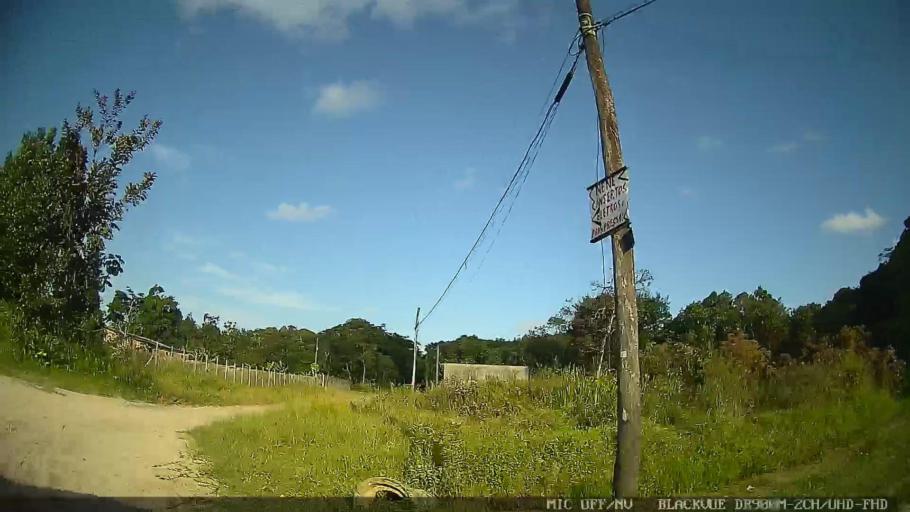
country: BR
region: Sao Paulo
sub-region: Itanhaem
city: Itanhaem
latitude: -24.1670
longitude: -46.8395
